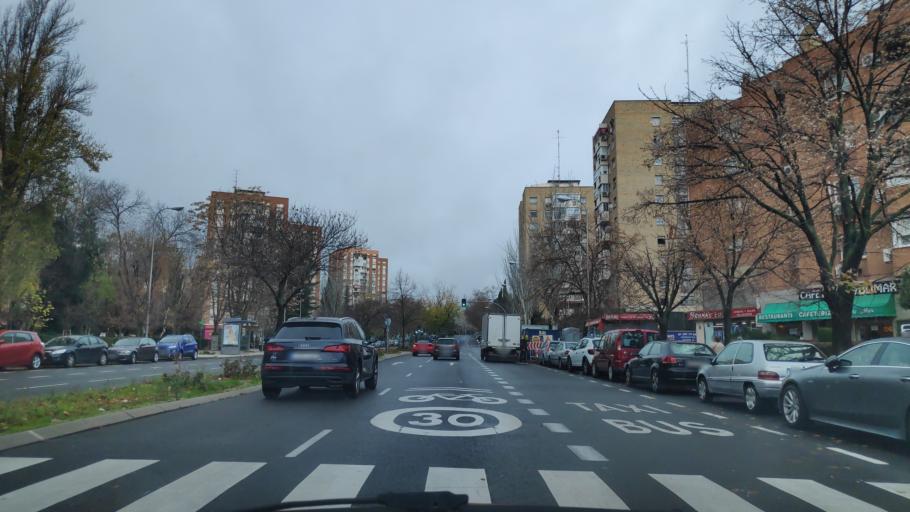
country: ES
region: Madrid
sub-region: Provincia de Madrid
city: Hortaleza
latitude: 40.4708
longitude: -3.6443
